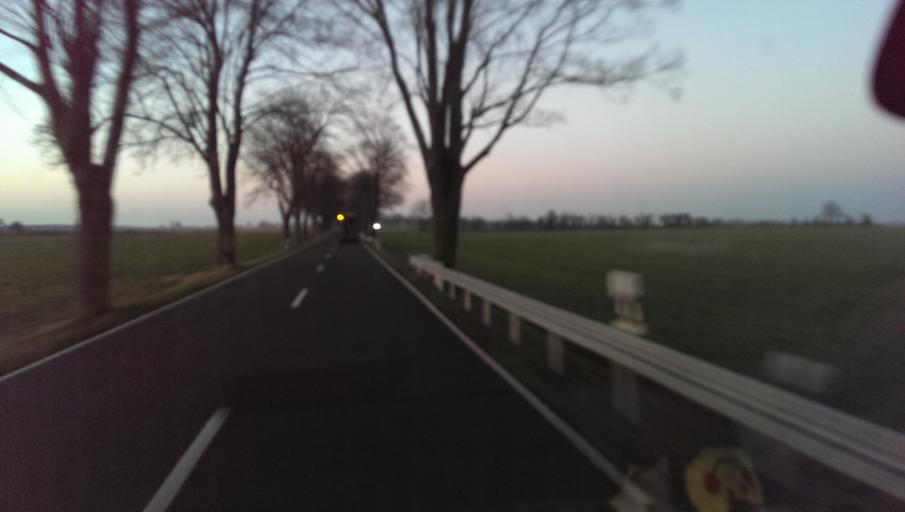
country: DE
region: Brandenburg
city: Juterbog
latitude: 51.9200
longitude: 13.1283
